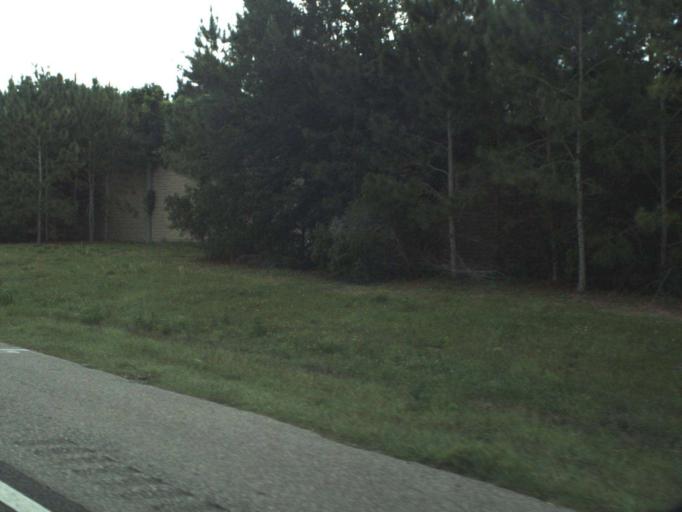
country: US
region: Florida
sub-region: Volusia County
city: Deltona
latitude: 28.8938
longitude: -81.2771
